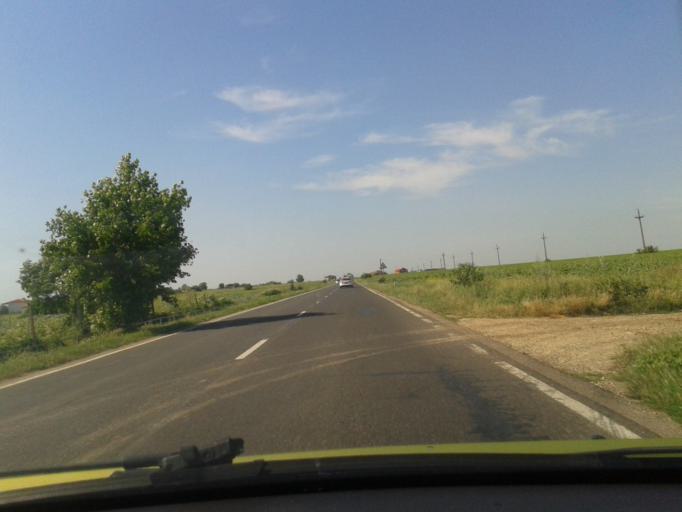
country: RO
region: Constanta
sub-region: Municipiul Mangalia
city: Mangalia
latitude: 43.7698
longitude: 28.5755
